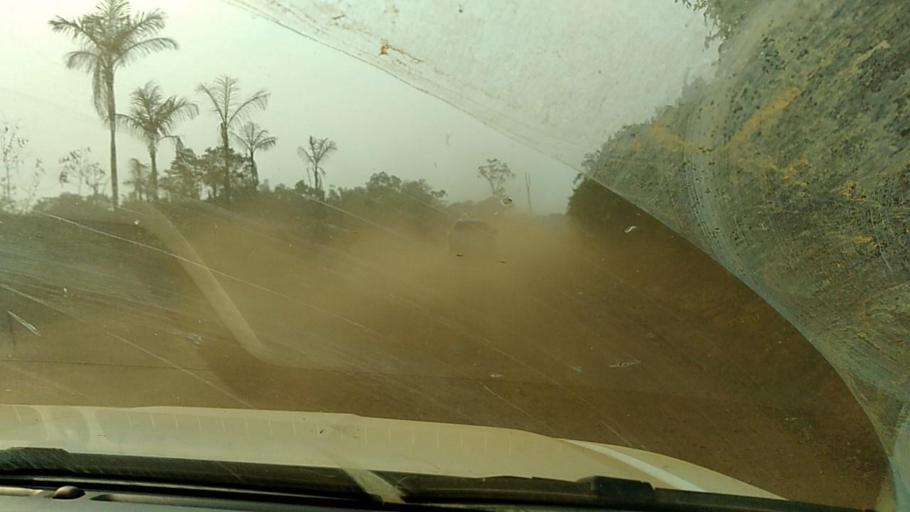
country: BR
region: Rondonia
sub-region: Porto Velho
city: Porto Velho
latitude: -8.7402
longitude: -63.9673
